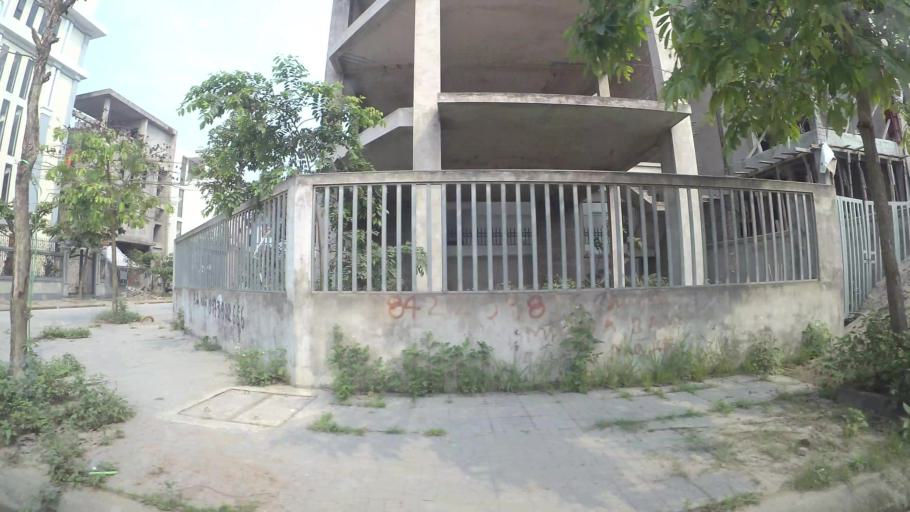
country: VN
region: Ha Noi
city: Thanh Xuan
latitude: 20.9852
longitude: 105.8030
